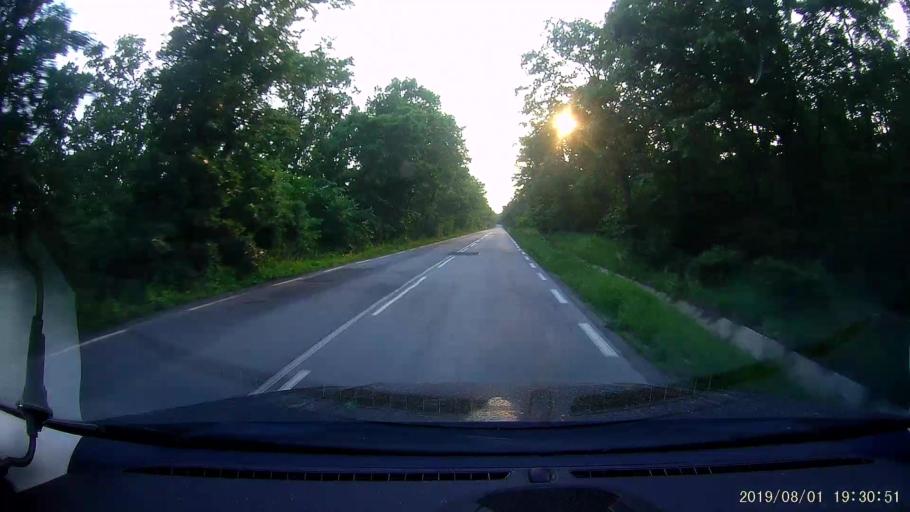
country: BG
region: Burgas
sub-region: Obshtina Sungurlare
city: Sungurlare
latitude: 42.8095
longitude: 26.8862
